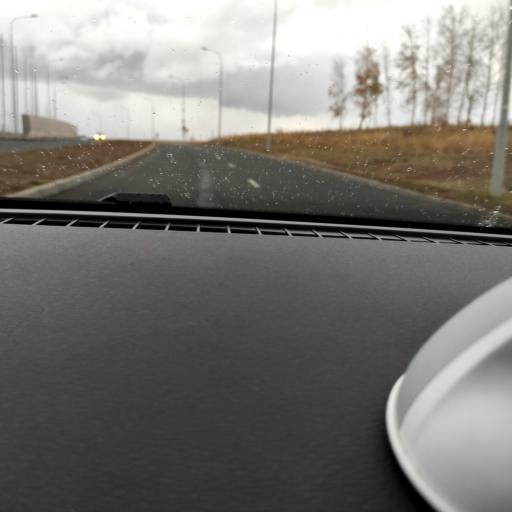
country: RU
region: Samara
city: Samara
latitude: 53.2818
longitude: 50.2381
